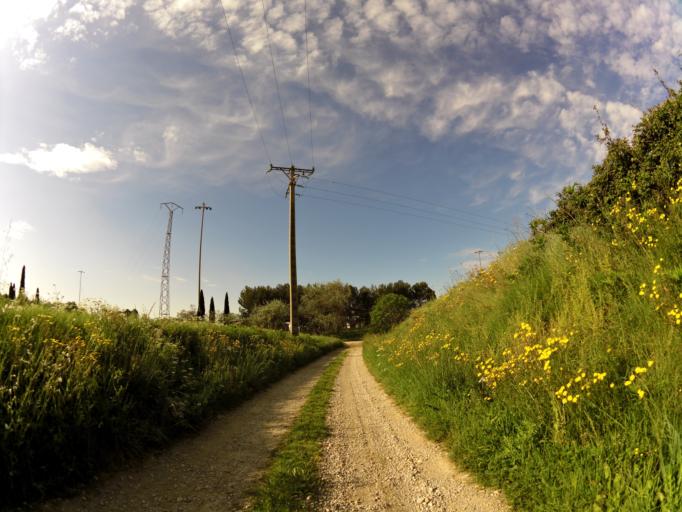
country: FR
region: Languedoc-Roussillon
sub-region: Departement du Gard
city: Aigues-Vives
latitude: 43.7285
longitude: 4.1829
